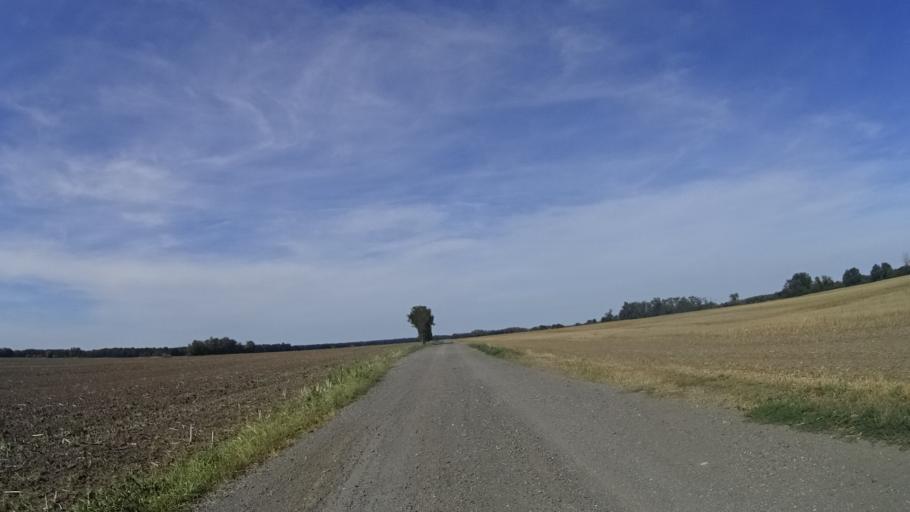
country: AT
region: Lower Austria
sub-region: Politischer Bezirk Ganserndorf
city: Durnkrut
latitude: 48.4344
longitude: 16.8711
